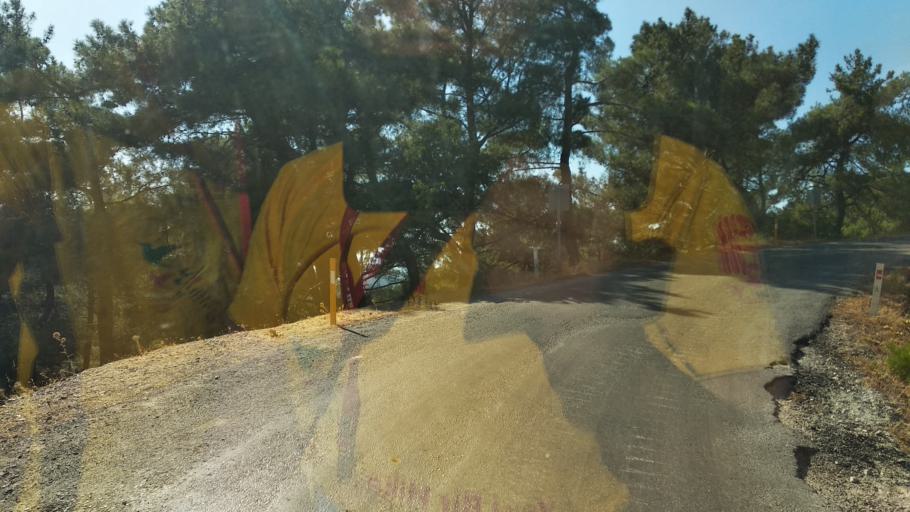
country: TR
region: Izmir
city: Gaziemir
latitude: 38.2959
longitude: 26.9998
